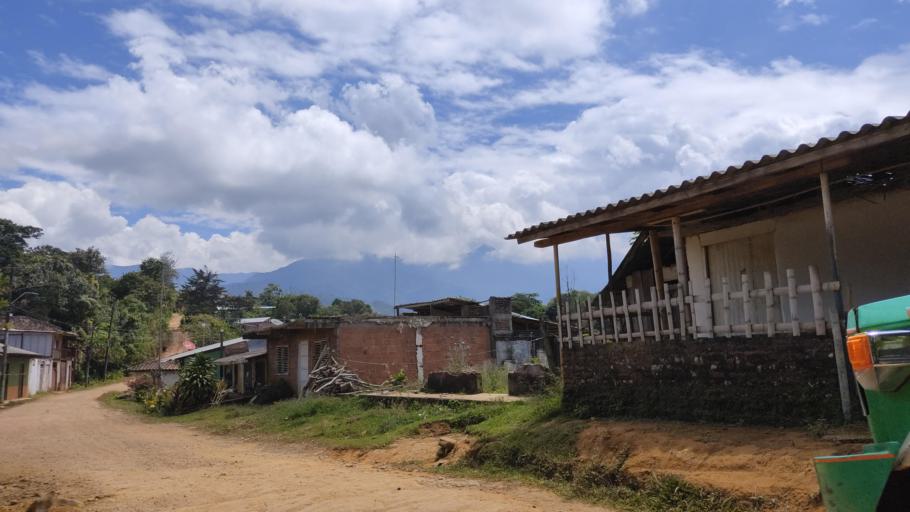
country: CO
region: Valle del Cauca
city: Jamundi
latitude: 3.2122
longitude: -76.6555
